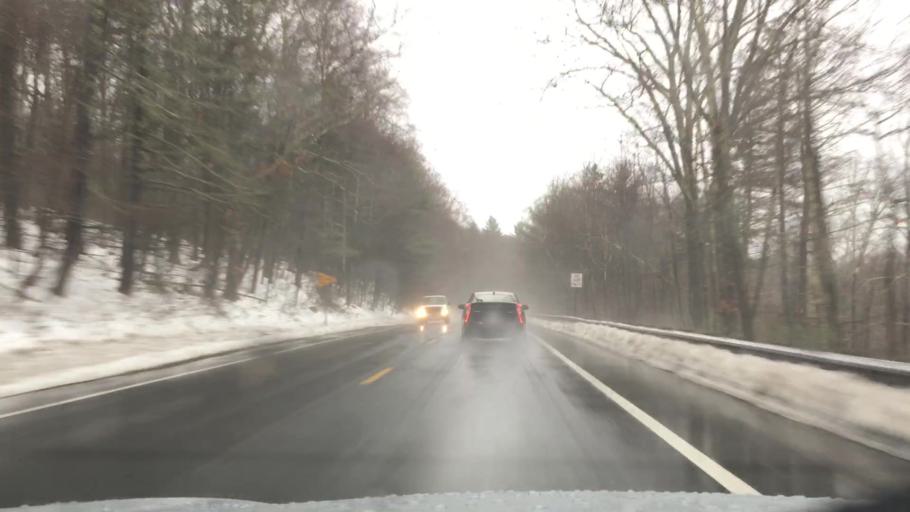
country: US
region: Massachusetts
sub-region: Franklin County
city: Shutesbury
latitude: 42.4458
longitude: -72.3880
